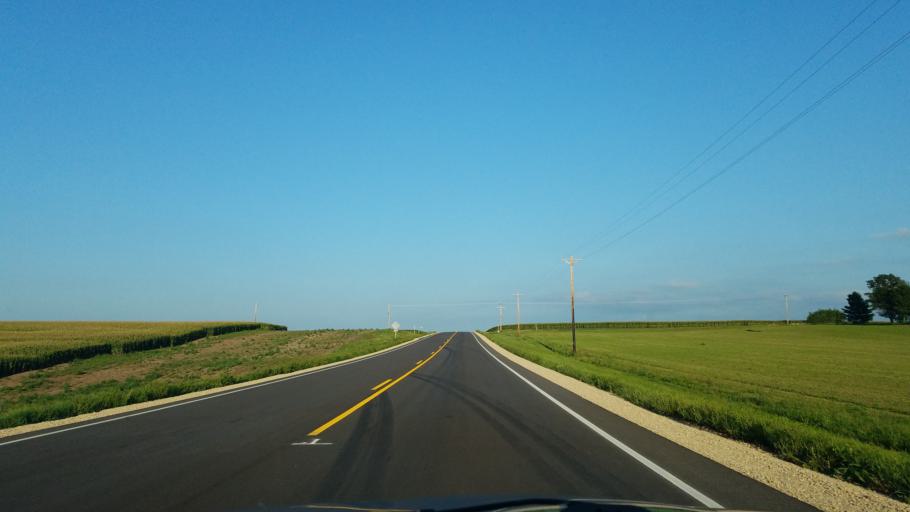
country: US
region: Wisconsin
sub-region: Saint Croix County
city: Hammond
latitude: 45.0792
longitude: -92.4191
